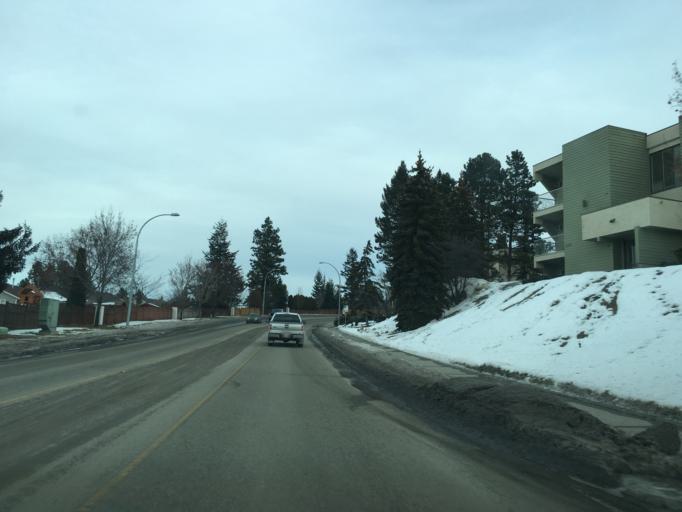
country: CA
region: British Columbia
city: Kamloops
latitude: 50.6486
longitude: -120.3635
